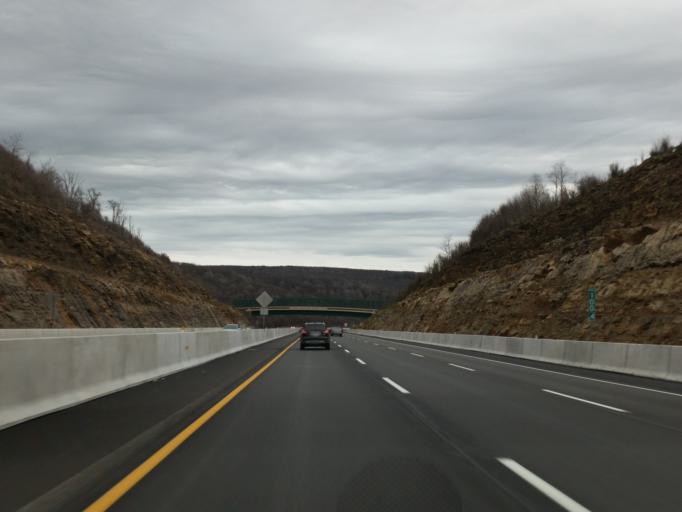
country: US
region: Pennsylvania
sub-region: Westmoreland County
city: Ligonier
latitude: 40.1056
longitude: -79.2126
